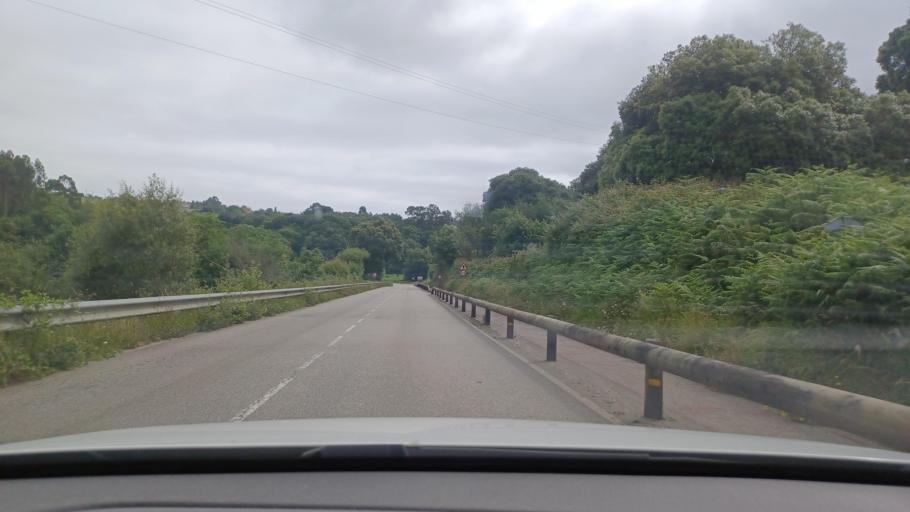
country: ES
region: Asturias
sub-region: Province of Asturias
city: Ribadesella
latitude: 43.4564
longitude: -5.0959
